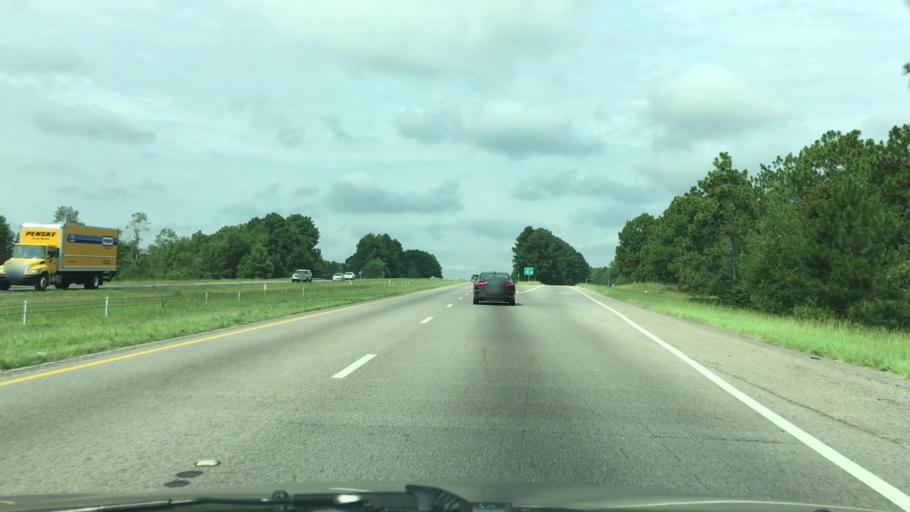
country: US
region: South Carolina
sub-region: Aiken County
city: Aiken
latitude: 33.6415
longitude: -81.7346
